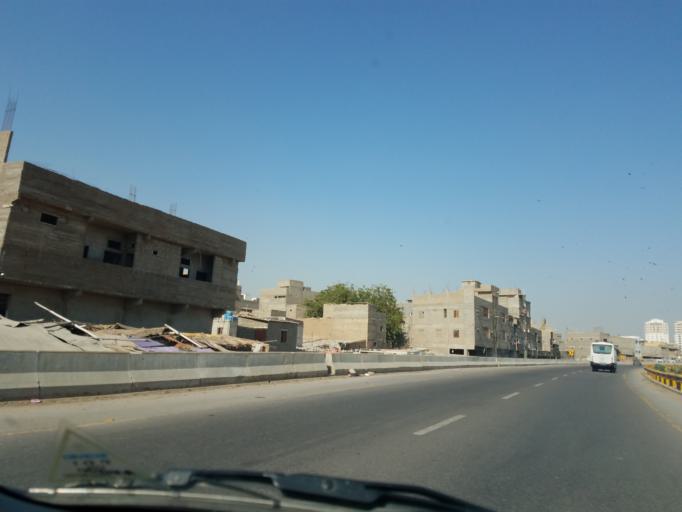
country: PK
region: Sindh
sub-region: Karachi District
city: Karachi
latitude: 24.9103
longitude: 67.0662
